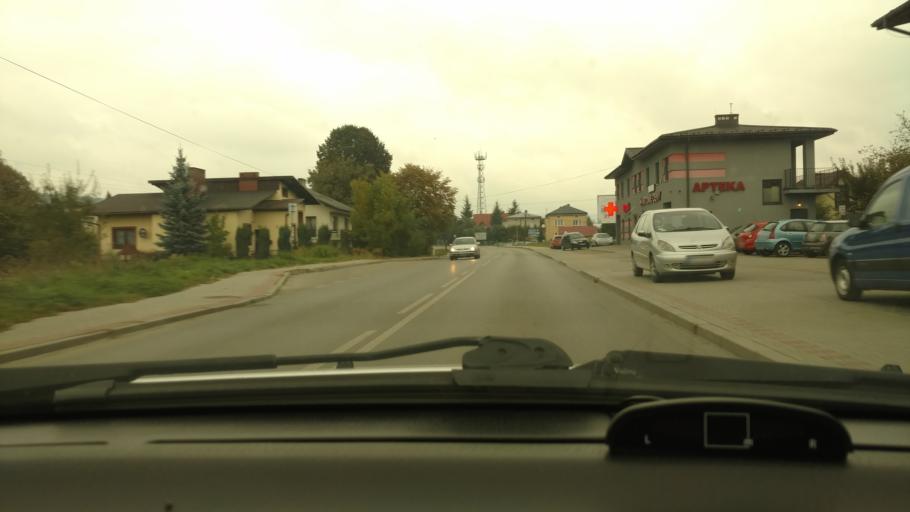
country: PL
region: Lesser Poland Voivodeship
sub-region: Powiat nowosadecki
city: Chelmiec
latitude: 49.6241
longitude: 20.6678
